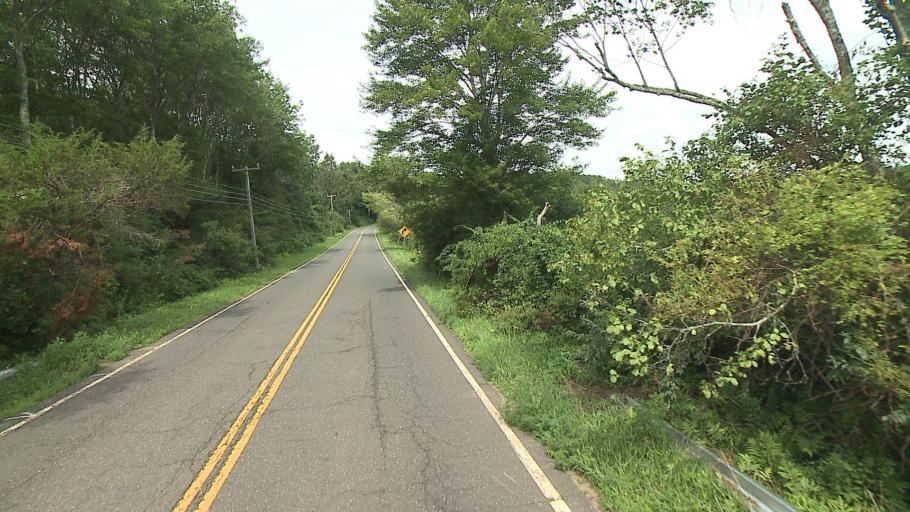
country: US
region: Connecticut
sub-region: Litchfield County
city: Woodbury
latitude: 41.5572
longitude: -73.2816
